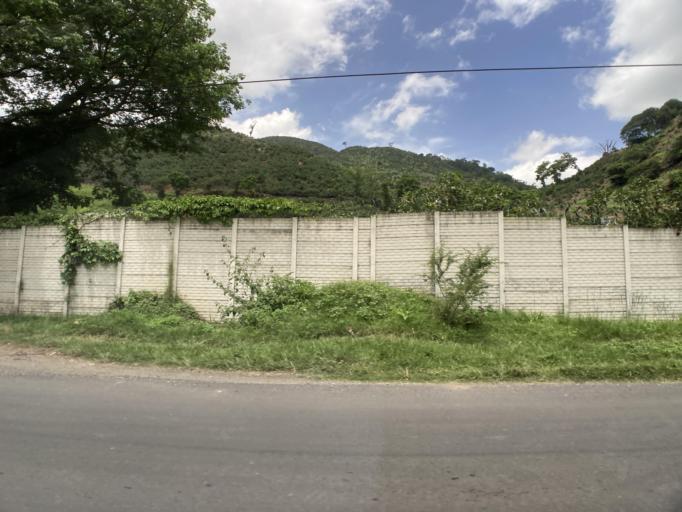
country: GT
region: Guatemala
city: Amatitlan
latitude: 14.4610
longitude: -90.5859
